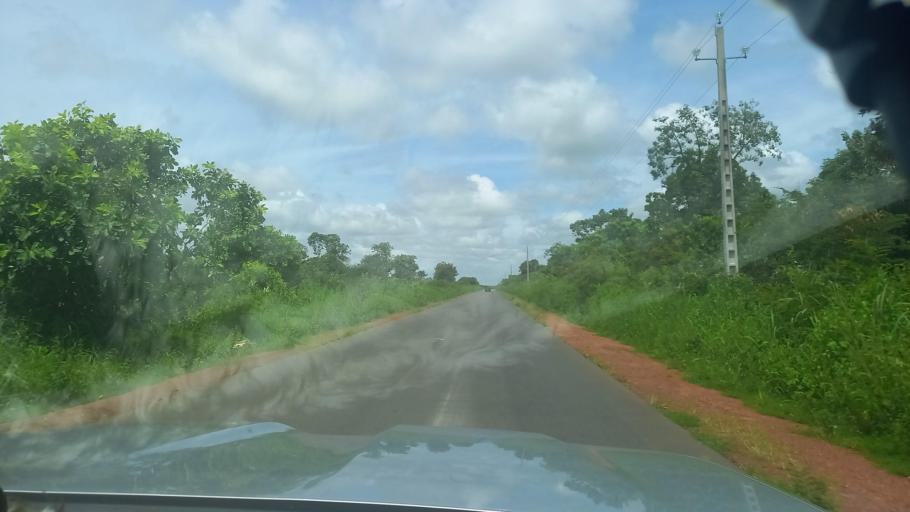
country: GM
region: Lower River
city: Kaiaf
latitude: 13.1879
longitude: -15.5575
